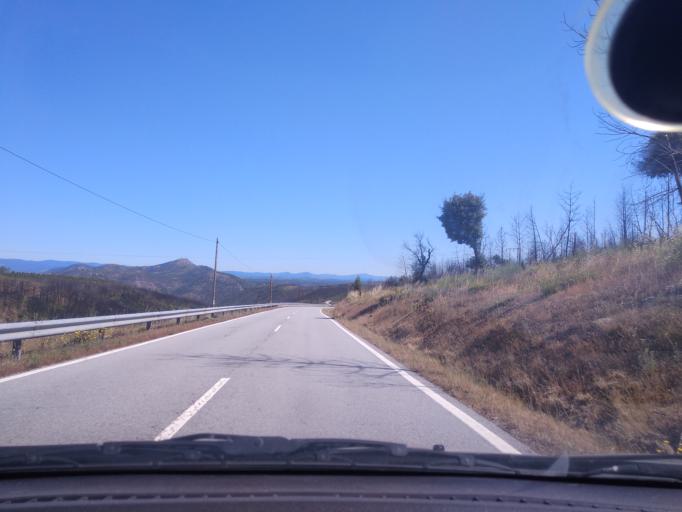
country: PT
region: Portalegre
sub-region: Nisa
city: Nisa
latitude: 39.6139
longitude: -7.6630
